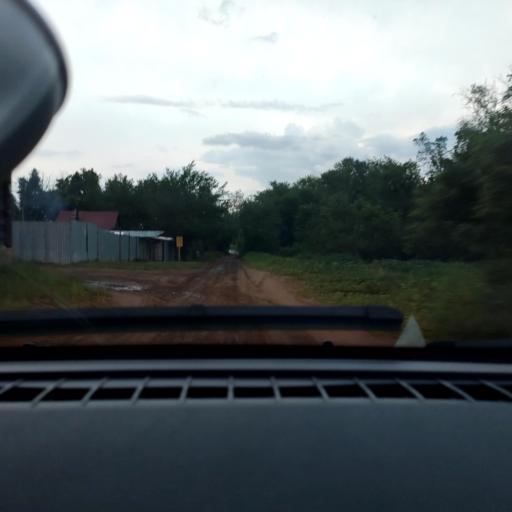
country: RU
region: Samara
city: Samara
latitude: 53.1271
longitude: 50.1881
